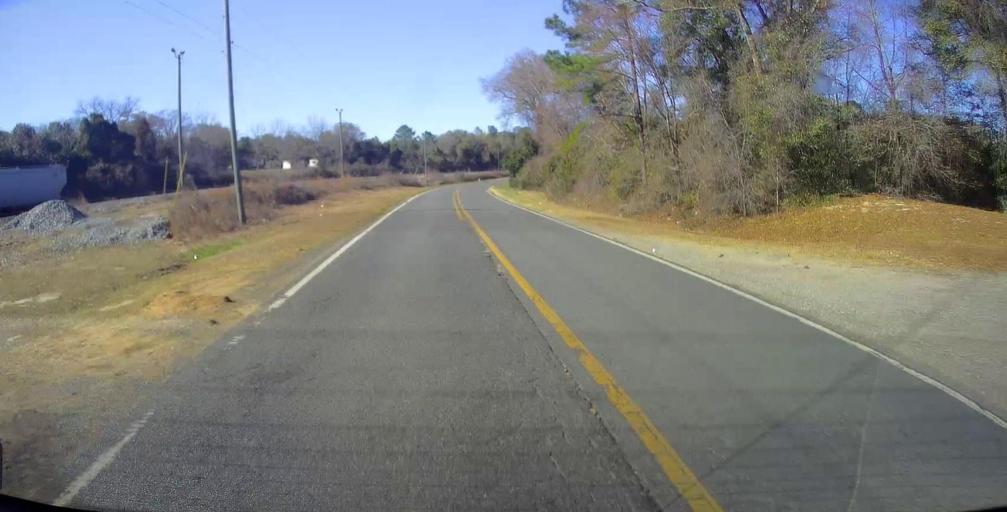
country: US
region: Georgia
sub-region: Macon County
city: Oglethorpe
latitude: 32.3002
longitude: -84.0617
